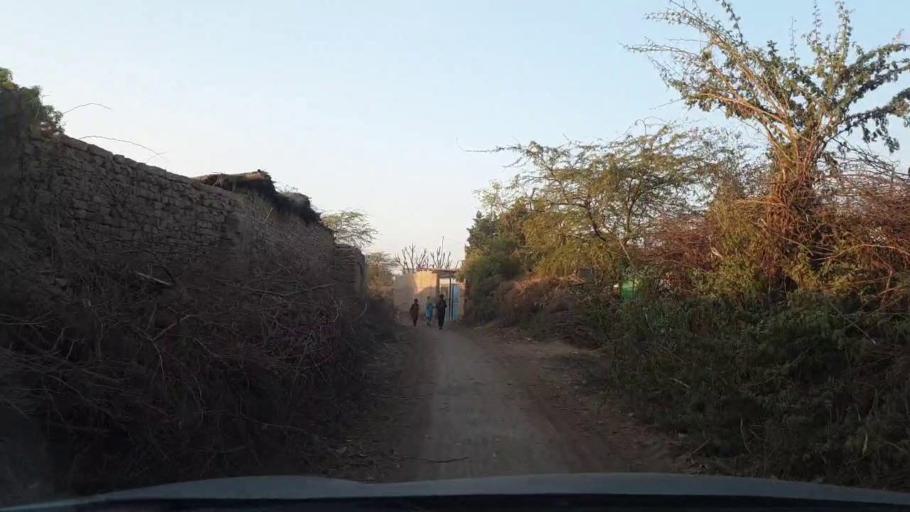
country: PK
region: Sindh
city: Tando Adam
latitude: 25.6806
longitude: 68.7437
